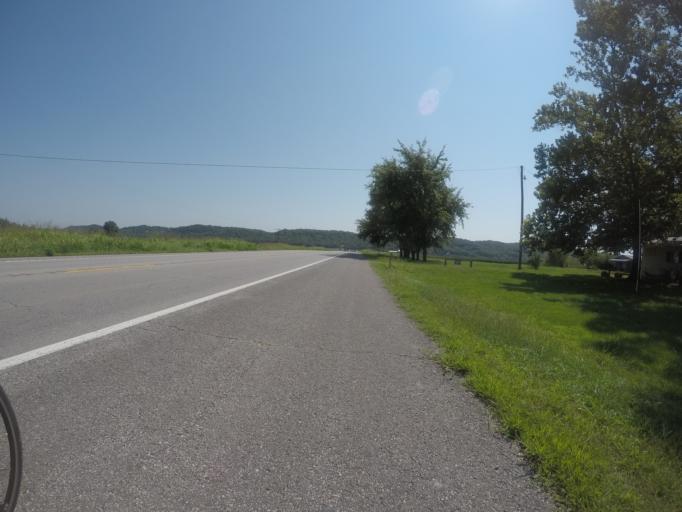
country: US
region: Kansas
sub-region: Atchison County
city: Atchison
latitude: 39.5566
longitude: -95.0569
